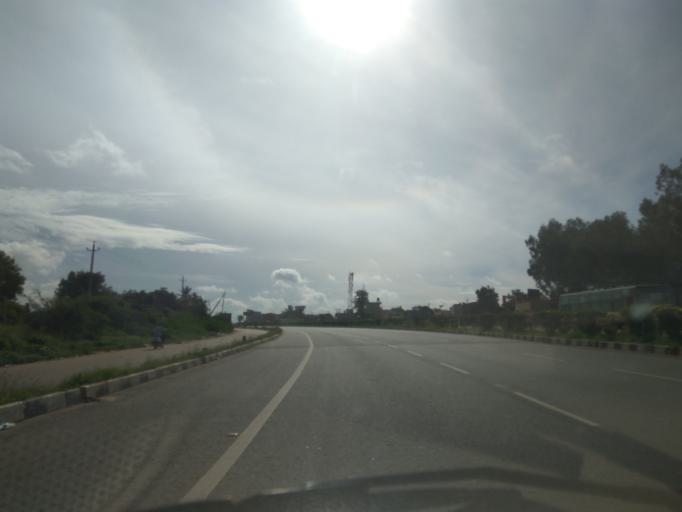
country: IN
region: Karnataka
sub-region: Bangalore Rural
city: Hoskote
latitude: 13.0770
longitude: 77.8057
